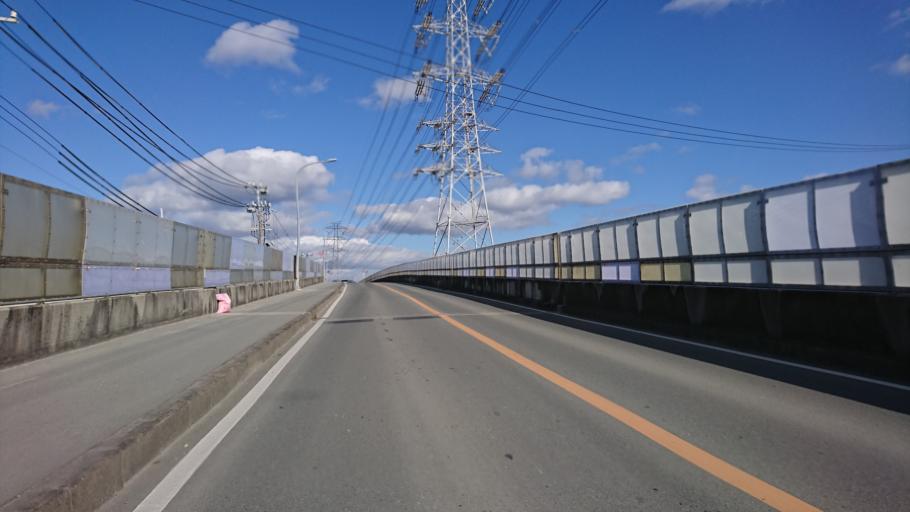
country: JP
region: Hyogo
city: Kakogawacho-honmachi
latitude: 34.7726
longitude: 134.7769
